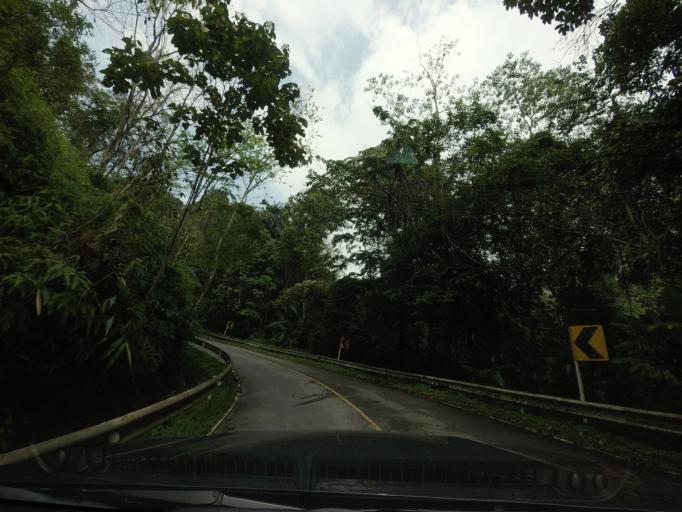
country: TH
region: Nan
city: Bo Kluea
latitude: 19.2059
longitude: 101.0718
